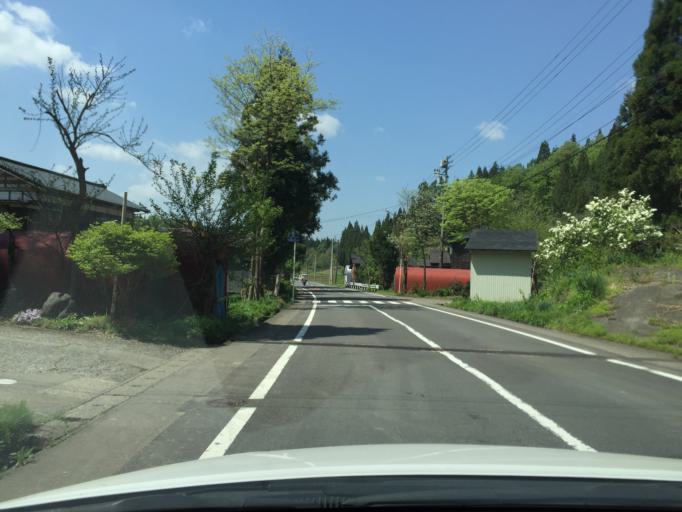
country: JP
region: Niigata
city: Tochio-honcho
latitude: 37.5093
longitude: 139.0750
